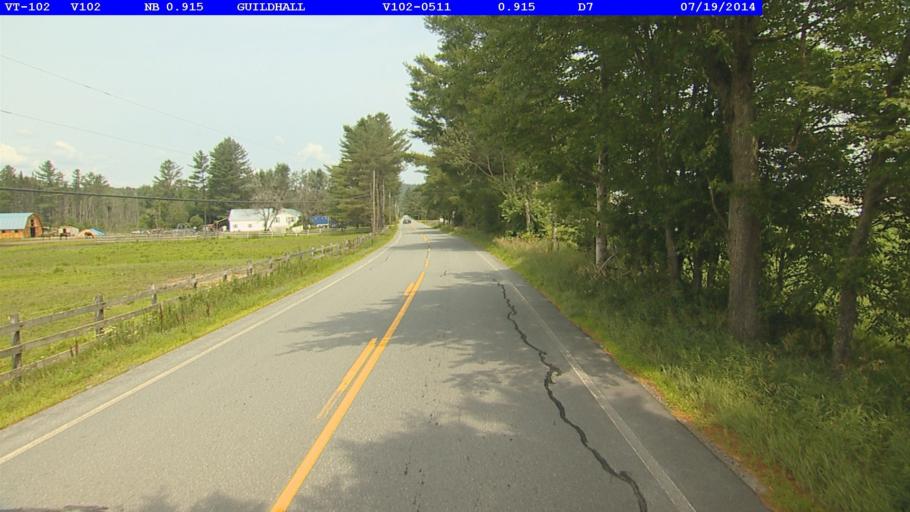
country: US
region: New Hampshire
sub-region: Coos County
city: Lancaster
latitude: 44.5086
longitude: -71.5937
